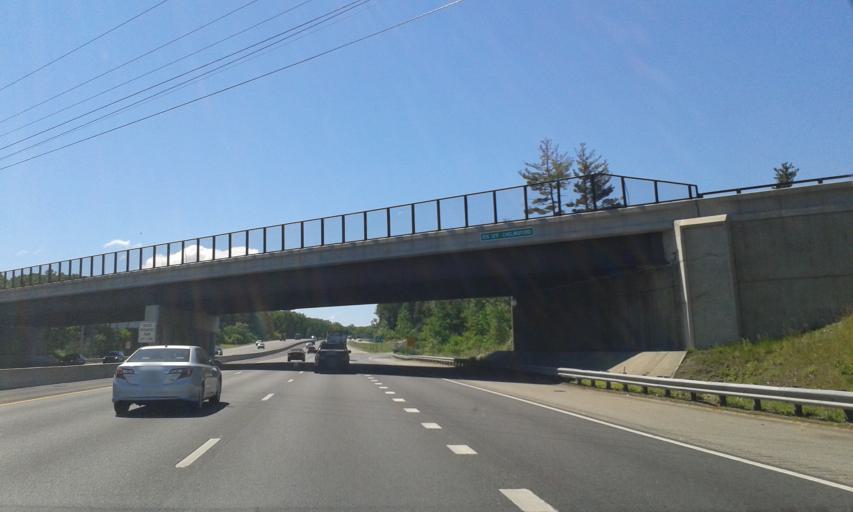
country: US
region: Massachusetts
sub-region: Middlesex County
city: Lowell
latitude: 42.5897
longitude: -71.3138
